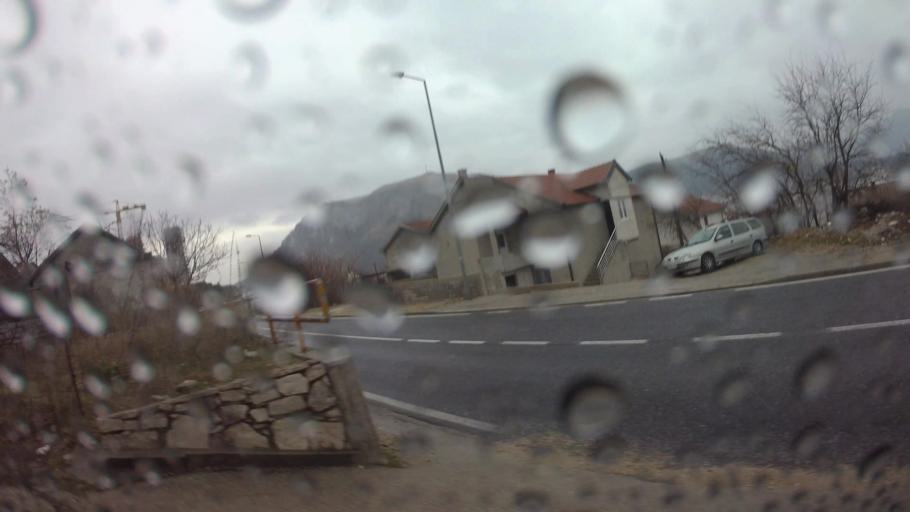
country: BA
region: Federation of Bosnia and Herzegovina
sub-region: Hercegovacko-Bosanski Kanton
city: Mostar
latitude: 43.3411
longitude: 17.8185
